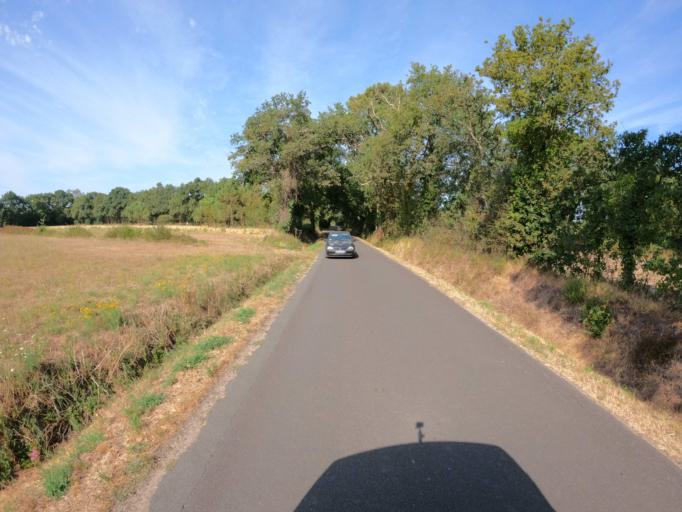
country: FR
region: Pays de la Loire
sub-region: Departement de la Vendee
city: Challans
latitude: 46.8076
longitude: -1.8589
